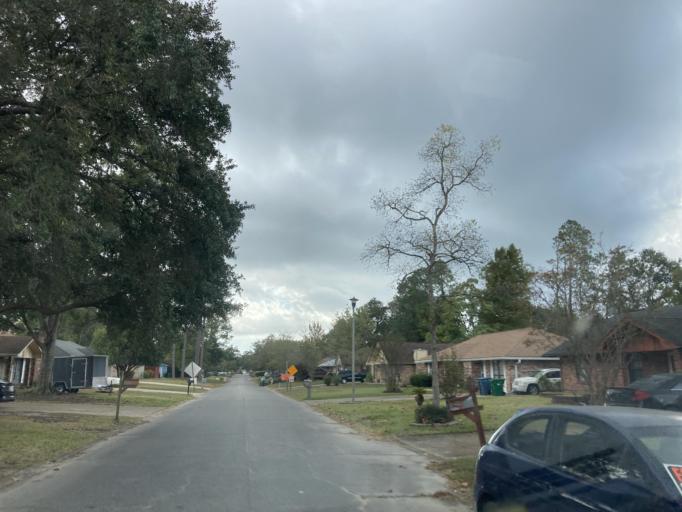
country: US
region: Mississippi
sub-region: Jackson County
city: Gulf Hills
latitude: 30.4386
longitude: -88.8200
